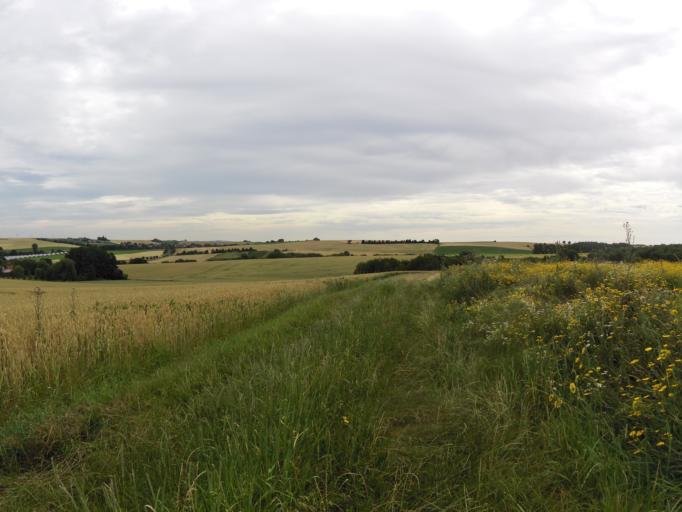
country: DE
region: Bavaria
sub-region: Regierungsbezirk Unterfranken
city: Reichenberg
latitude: 49.7158
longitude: 9.9061
